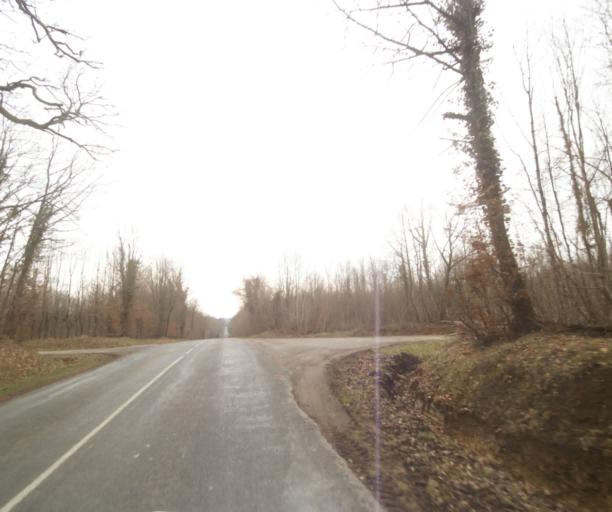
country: FR
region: Champagne-Ardenne
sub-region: Departement de la Haute-Marne
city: Villiers-en-Lieu
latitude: 48.7066
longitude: 4.8917
